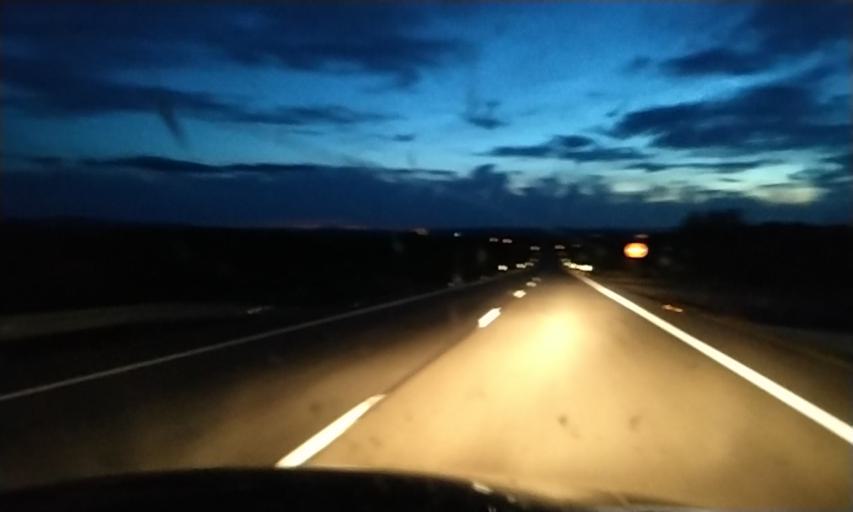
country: ES
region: Extremadura
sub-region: Provincia de Caceres
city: Galisteo
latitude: 39.9782
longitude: -6.2124
